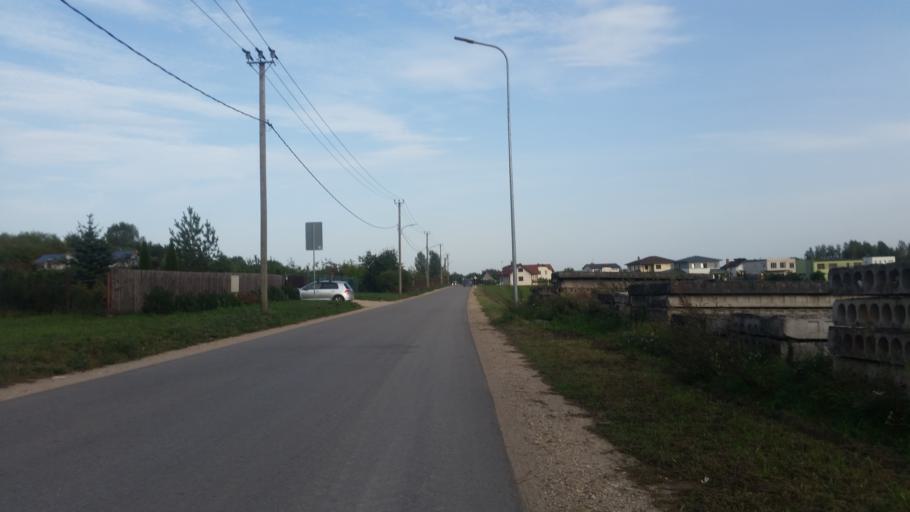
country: LV
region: Ikskile
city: Ikskile
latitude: 56.8198
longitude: 24.5078
